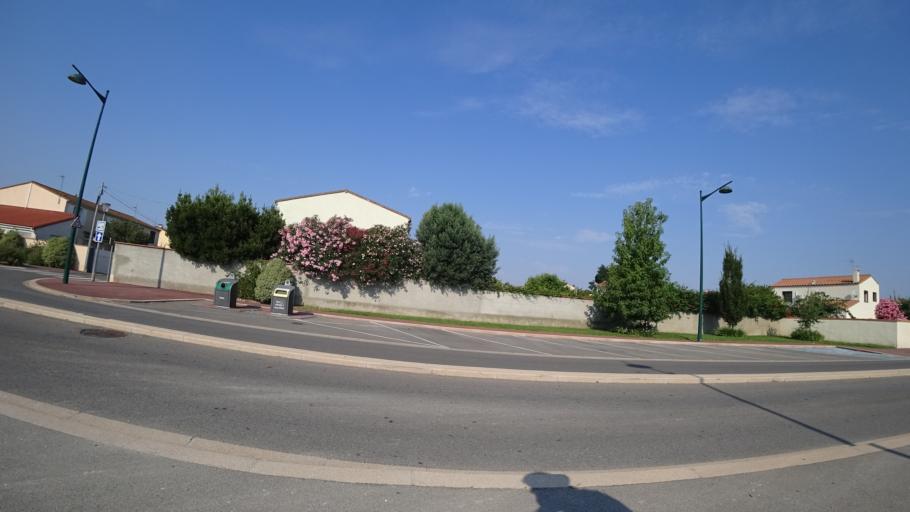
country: FR
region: Languedoc-Roussillon
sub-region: Departement des Pyrenees-Orientales
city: Bompas
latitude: 42.7234
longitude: 2.9378
